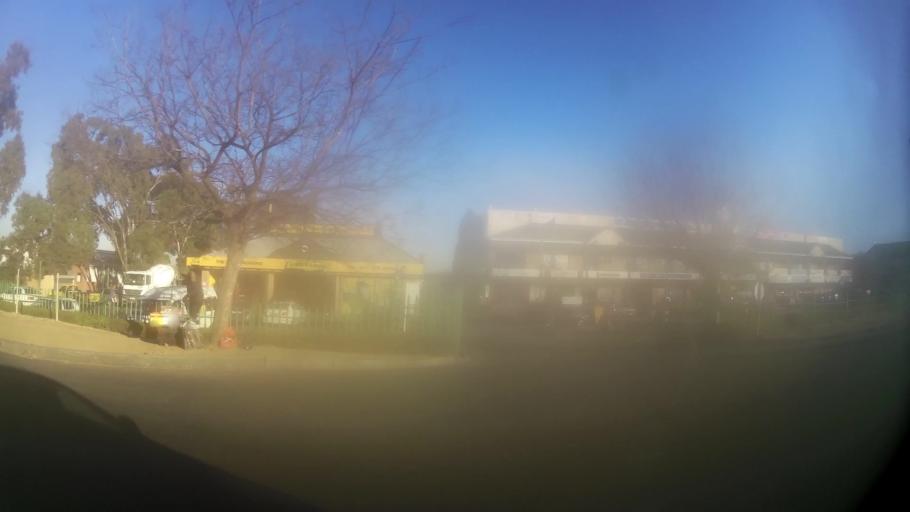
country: ZA
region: Gauteng
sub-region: City of Johannesburg Metropolitan Municipality
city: Midrand
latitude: -25.9911
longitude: 28.1300
